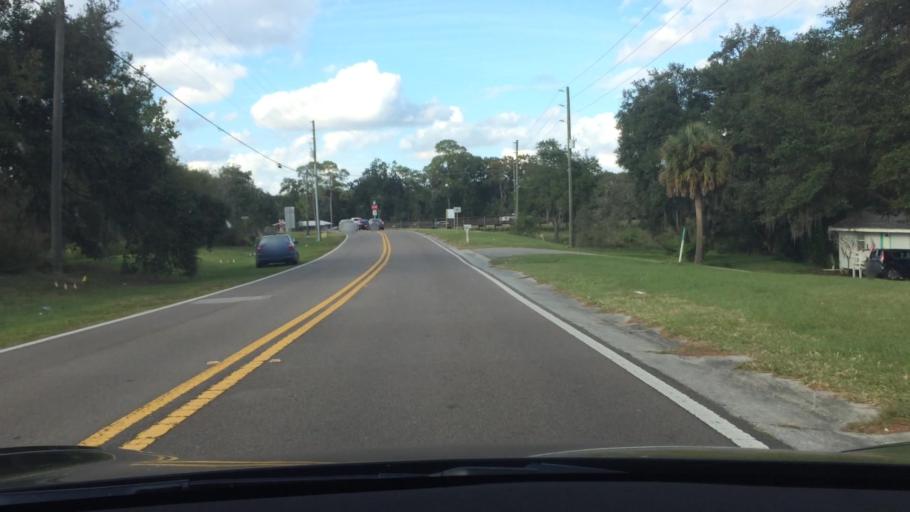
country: US
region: Florida
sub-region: Pasco County
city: Land O' Lakes
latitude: 28.1850
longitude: -82.4032
